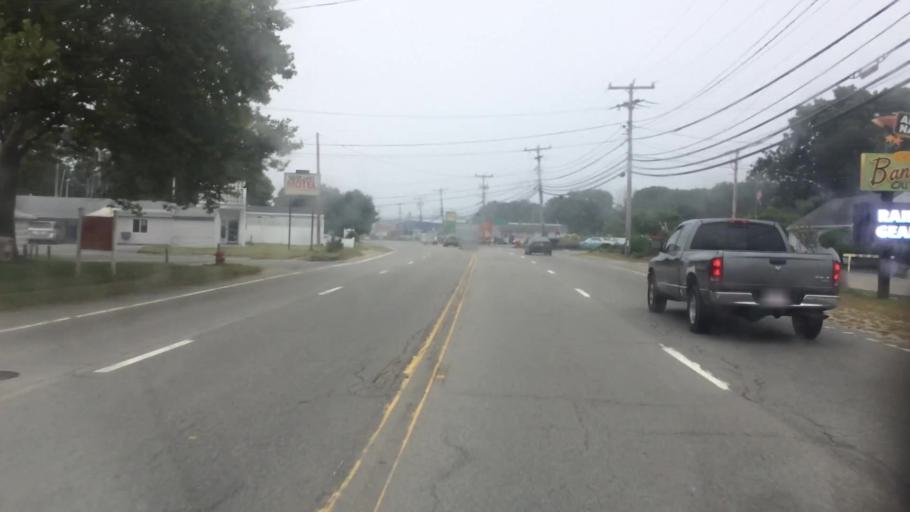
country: US
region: Massachusetts
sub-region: Plymouth County
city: Onset
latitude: 41.7584
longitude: -70.6604
